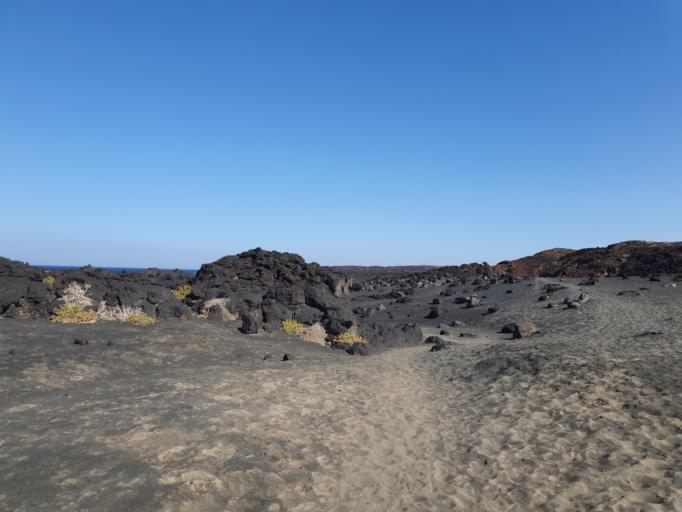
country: ES
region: Canary Islands
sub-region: Provincia de Las Palmas
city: Tinajo
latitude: 29.0654
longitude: -13.7630
